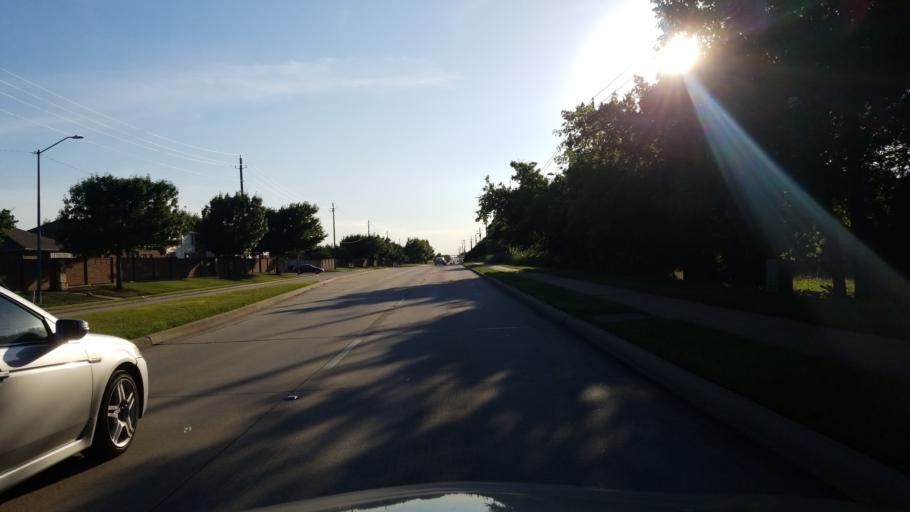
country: US
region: Texas
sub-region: Dallas County
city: Grand Prairie
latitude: 32.6914
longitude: -97.0365
